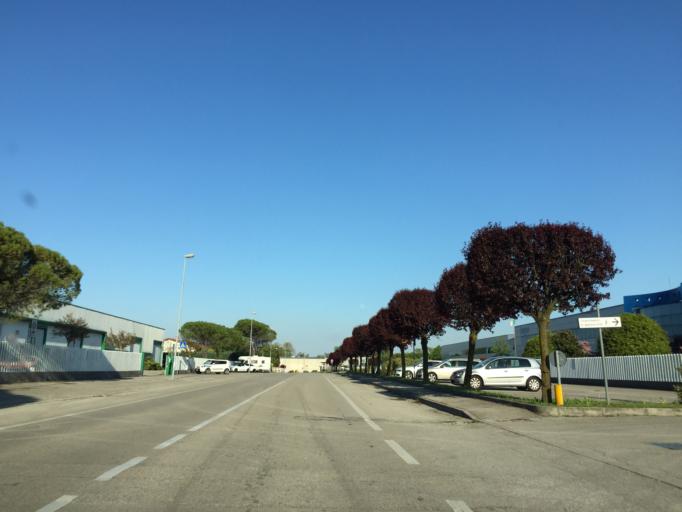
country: IT
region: Friuli Venezia Giulia
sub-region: Provincia di Pordenone
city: Porcia
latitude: 45.9580
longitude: 12.5940
